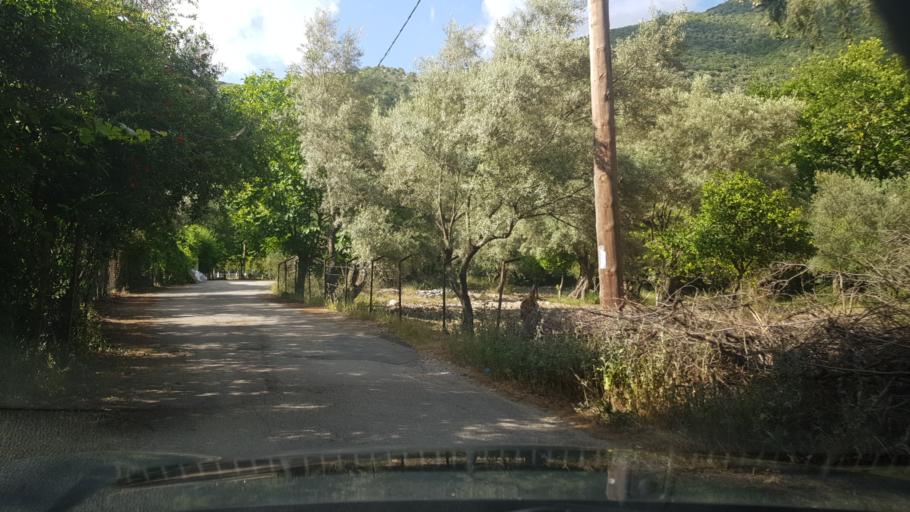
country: GR
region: Ionian Islands
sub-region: Lefkada
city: Nidri
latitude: 38.7191
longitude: 20.6951
